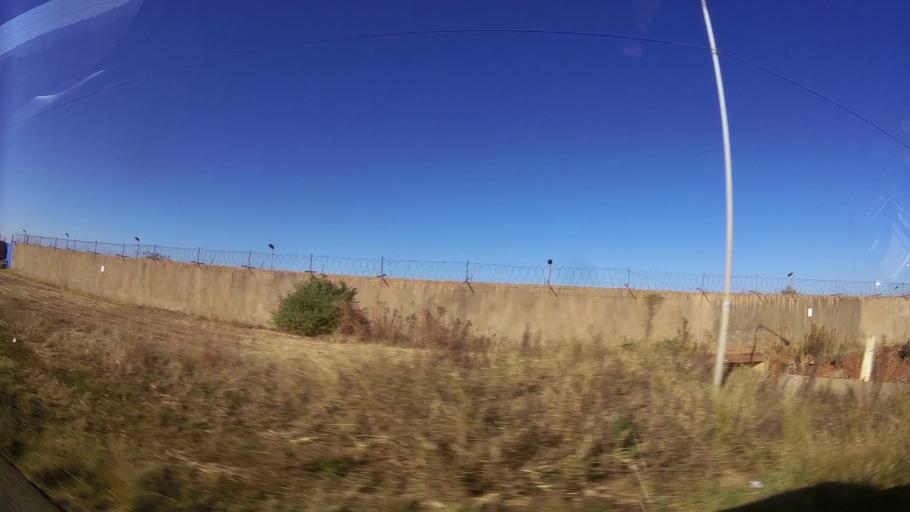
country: ZA
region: Gauteng
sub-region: City of Tshwane Metropolitan Municipality
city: Centurion
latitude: -25.8094
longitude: 28.2181
